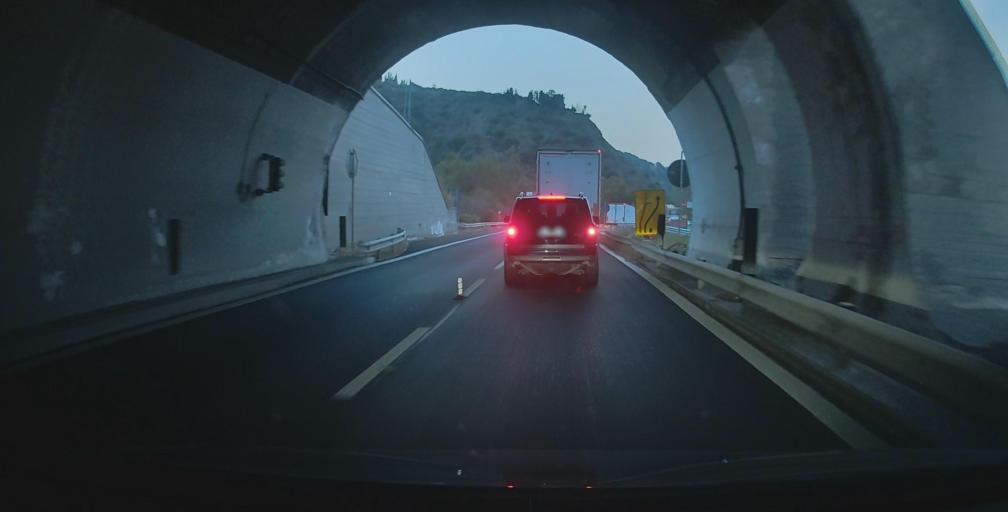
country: IT
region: Sicily
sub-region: Messina
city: Scaletta Zanclea
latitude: 38.0594
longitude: 15.4760
